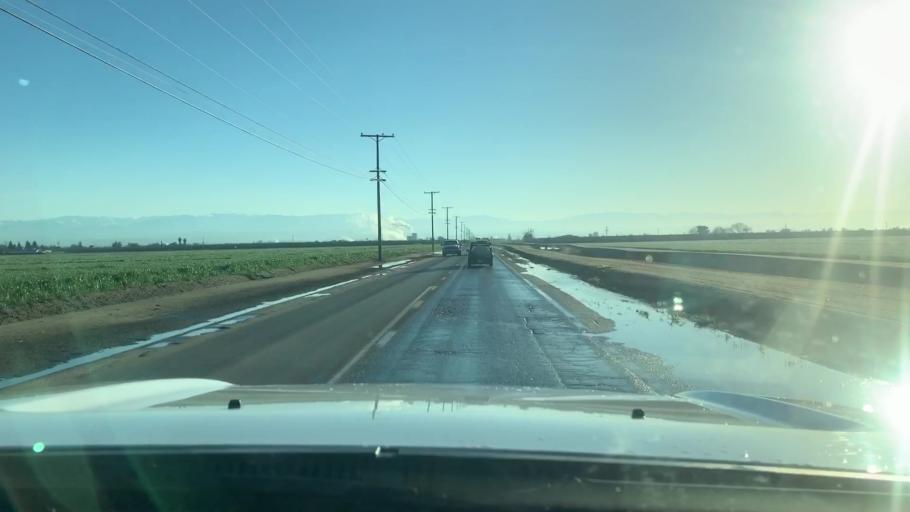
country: US
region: California
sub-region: Tulare County
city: Tulare
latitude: 36.1819
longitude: -119.3653
